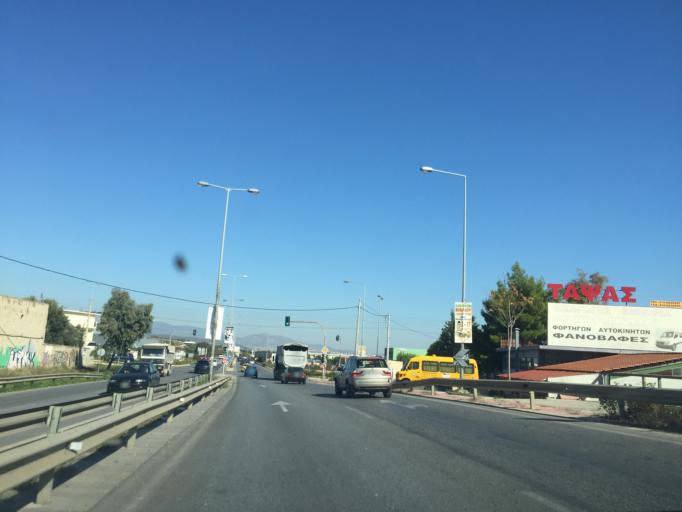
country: GR
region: Attica
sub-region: Nomarchia Anatolikis Attikis
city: Koropi
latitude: 37.8919
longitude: 23.8830
